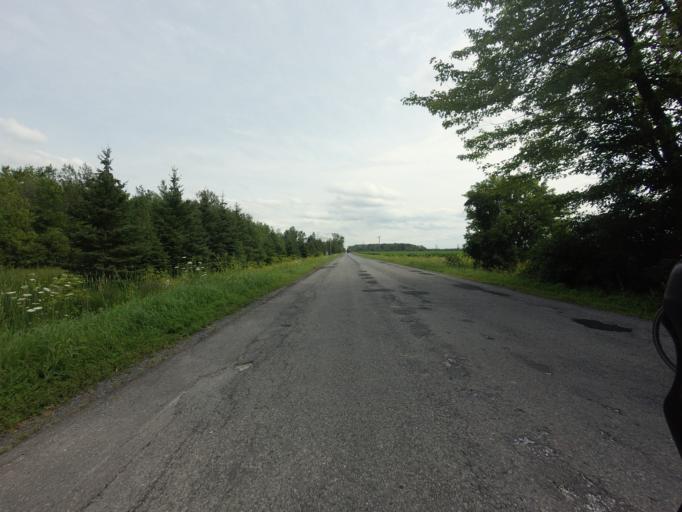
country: CA
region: Ontario
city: Bells Corners
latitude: 45.1139
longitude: -75.5991
